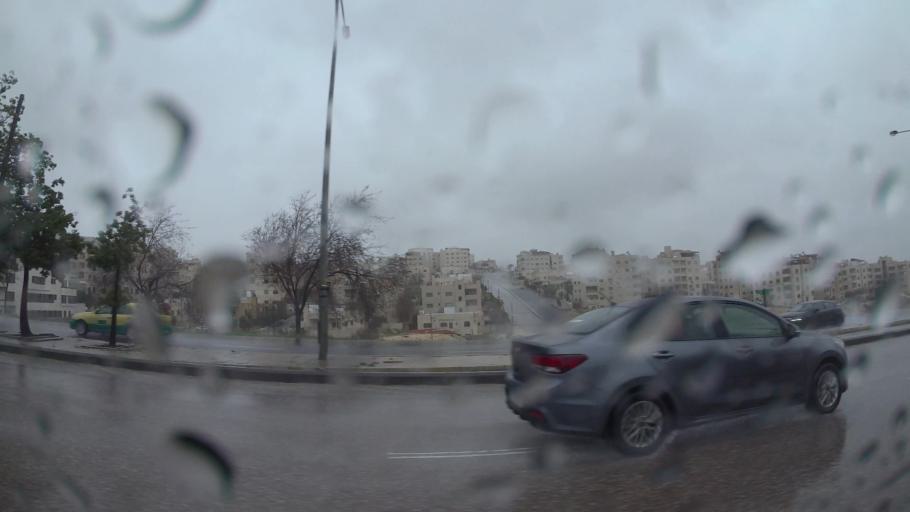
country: JO
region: Amman
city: Al Jubayhah
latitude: 32.0222
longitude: 35.8937
